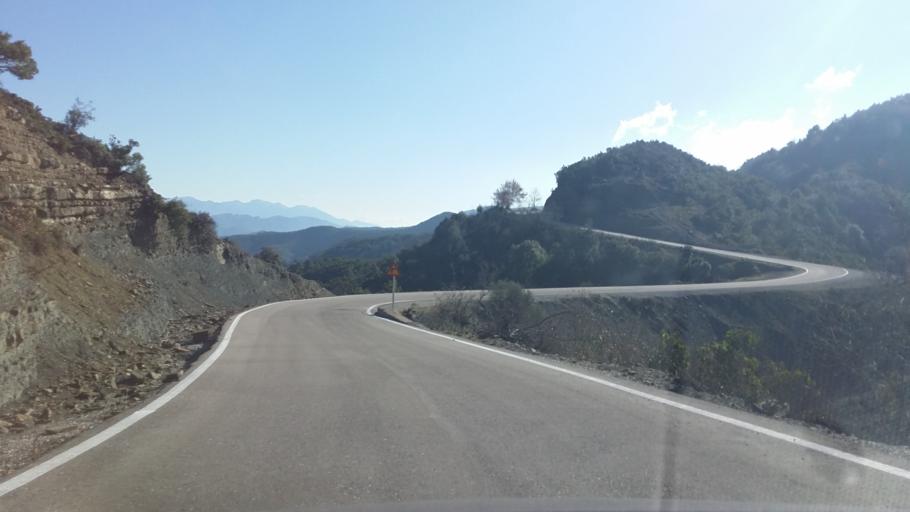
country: GR
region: West Greece
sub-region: Nomos Aitolias kai Akarnanias
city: Krikellos
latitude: 38.9915
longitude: 21.2770
